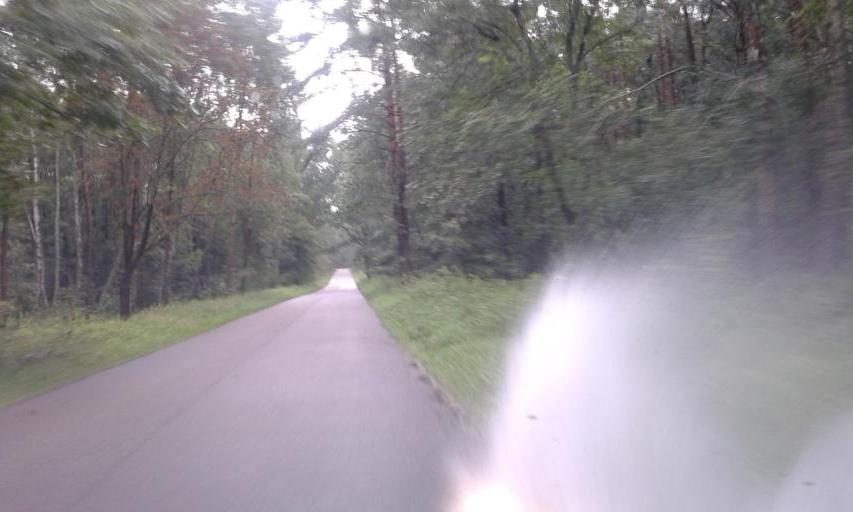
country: PL
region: West Pomeranian Voivodeship
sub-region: Powiat szczecinecki
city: Borne Sulinowo
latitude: 53.5320
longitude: 16.4943
